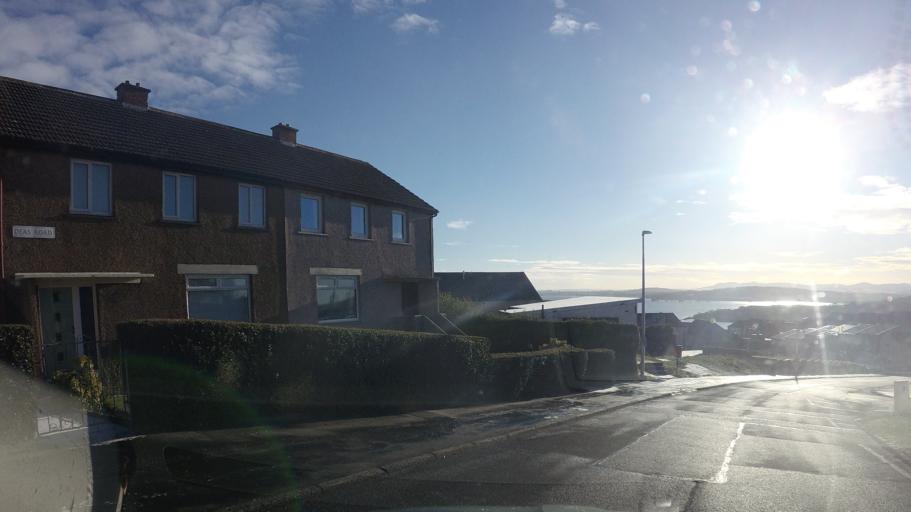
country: GB
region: Scotland
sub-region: Fife
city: Inverkeithing
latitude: 56.0324
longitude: -3.4019
